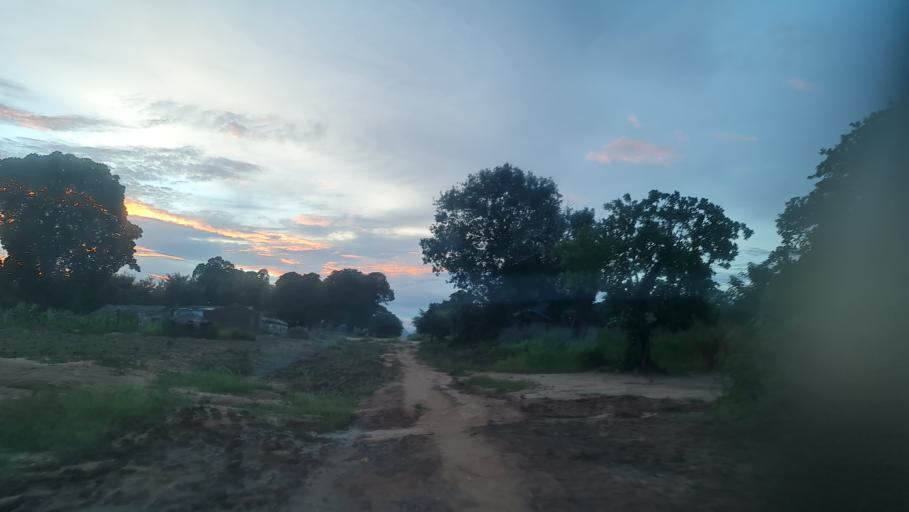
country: MZ
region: Nampula
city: Nampula
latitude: -14.7351
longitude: 39.9204
